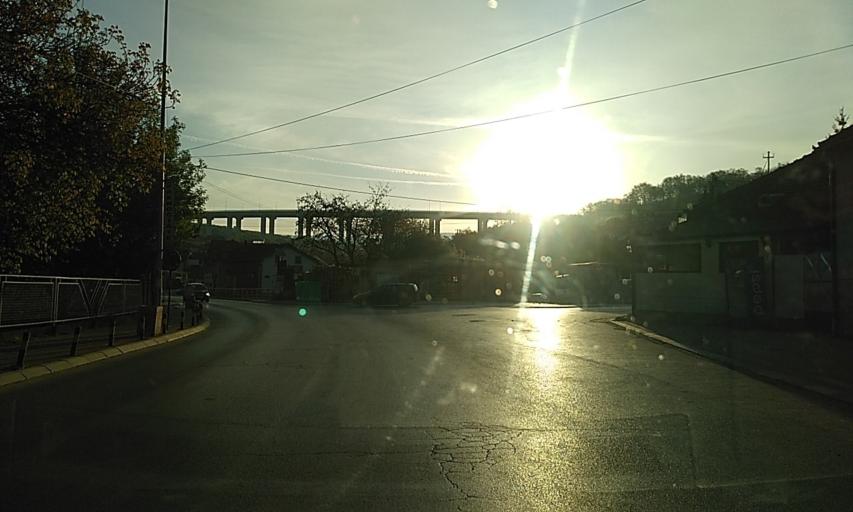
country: RS
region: Central Serbia
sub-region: Pcinjski Okrug
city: Vladicin Han
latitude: 42.7063
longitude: 22.0653
